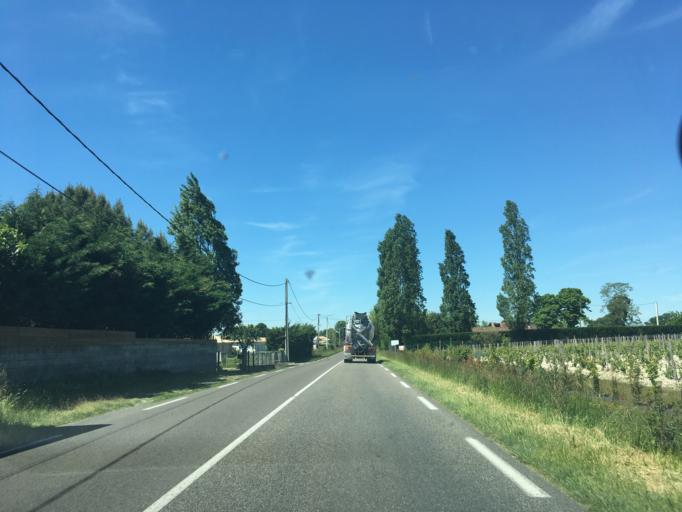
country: FR
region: Aquitaine
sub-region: Departement de la Gironde
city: Listrac-Medoc
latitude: 45.0784
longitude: -0.7945
